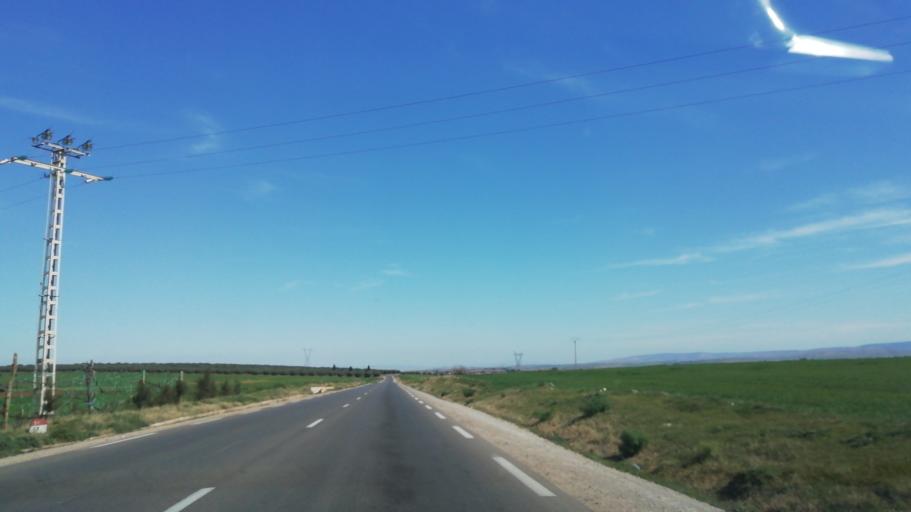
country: DZ
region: Mascara
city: Oued el Abtal
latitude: 35.4185
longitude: 0.4177
